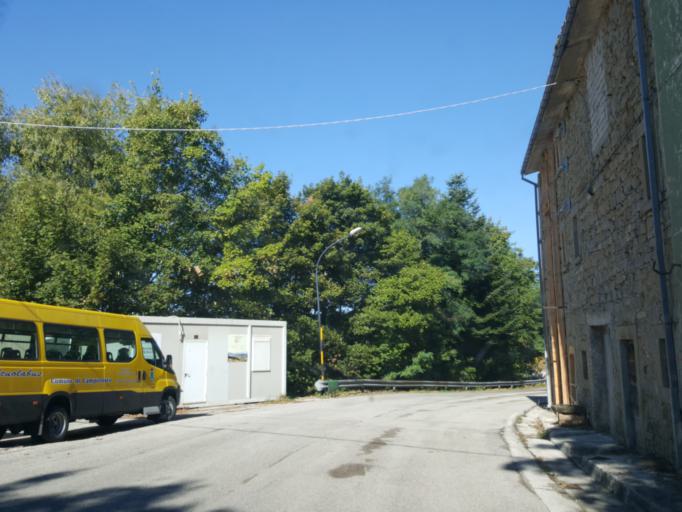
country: IT
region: Abruzzo
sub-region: Provincia dell' Aquila
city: Campotosto
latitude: 42.5576
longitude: 13.3663
